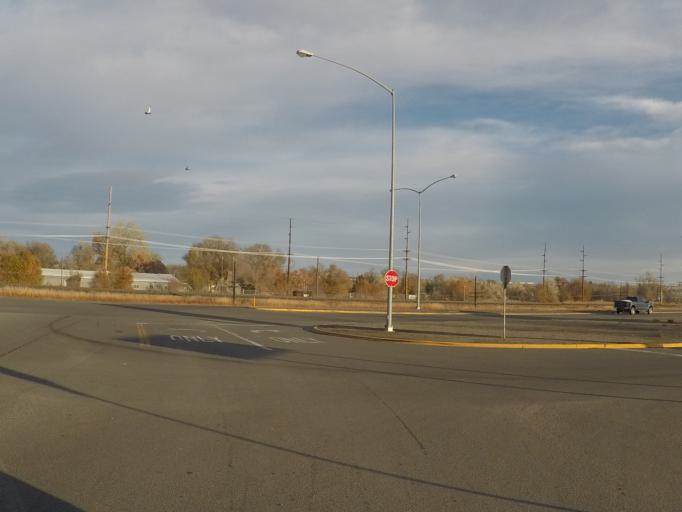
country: US
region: Montana
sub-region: Yellowstone County
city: Billings
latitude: 45.7632
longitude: -108.5392
